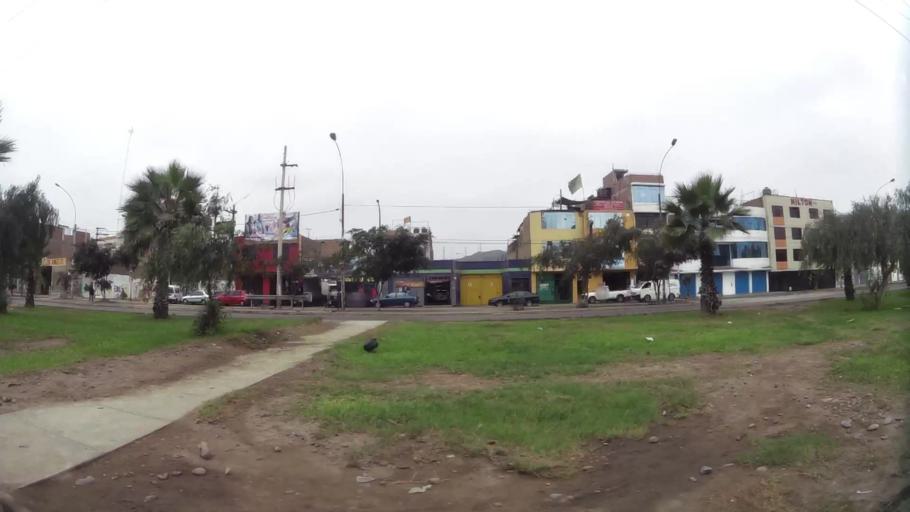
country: PE
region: Lima
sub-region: Lima
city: Independencia
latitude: -11.9940
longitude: -77.0837
